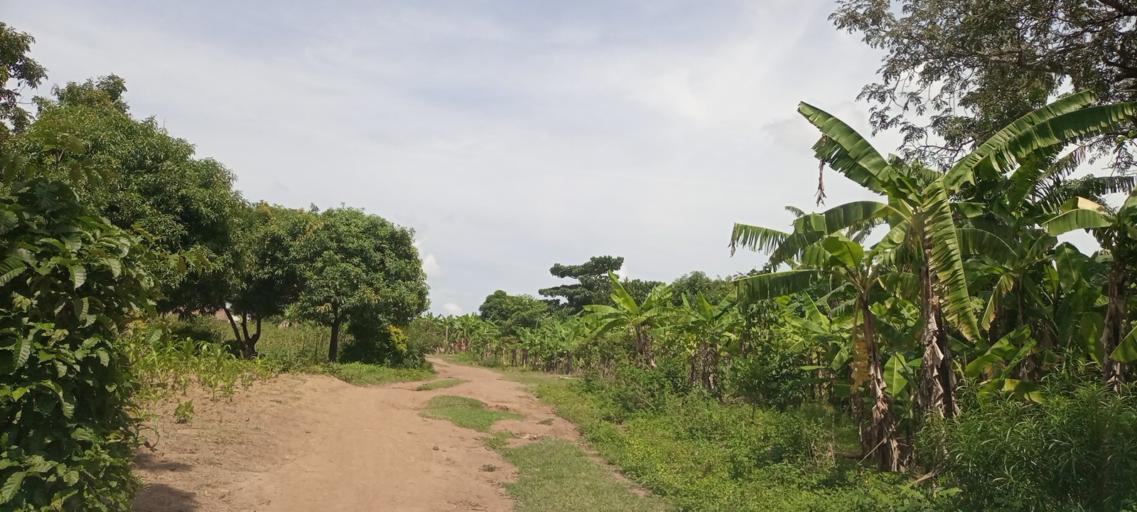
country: UG
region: Eastern Region
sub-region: Budaka District
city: Budaka
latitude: 1.1701
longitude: 33.9457
